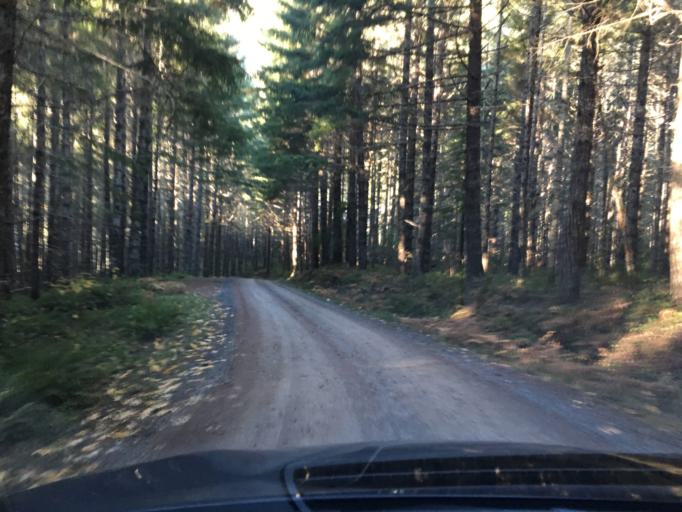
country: US
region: Oregon
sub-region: Douglas County
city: Winston
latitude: 43.3156
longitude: -123.5789
